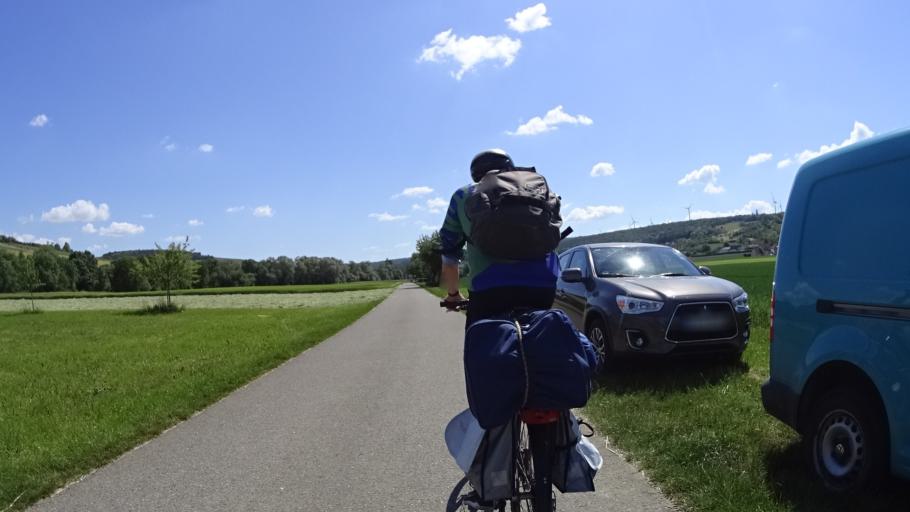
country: DE
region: Bavaria
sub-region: Regierungsbezirk Unterfranken
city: Tauberrettersheim
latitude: 49.4963
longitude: 9.9257
